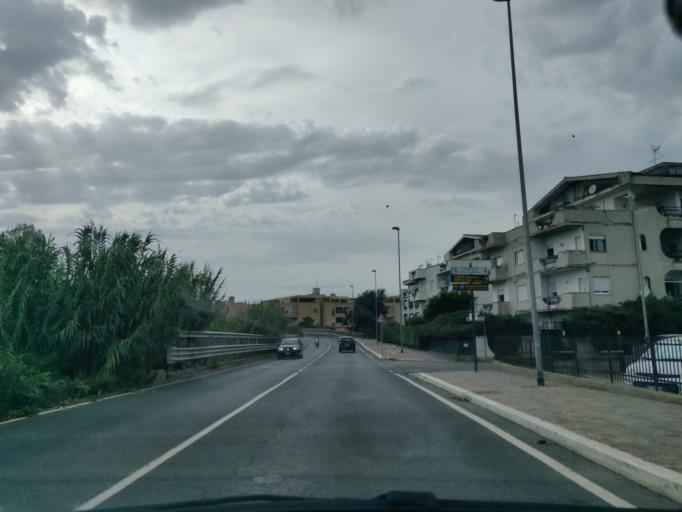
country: IT
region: Latium
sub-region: Citta metropolitana di Roma Capitale
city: Santa Marinella
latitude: 42.0402
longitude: 11.8844
